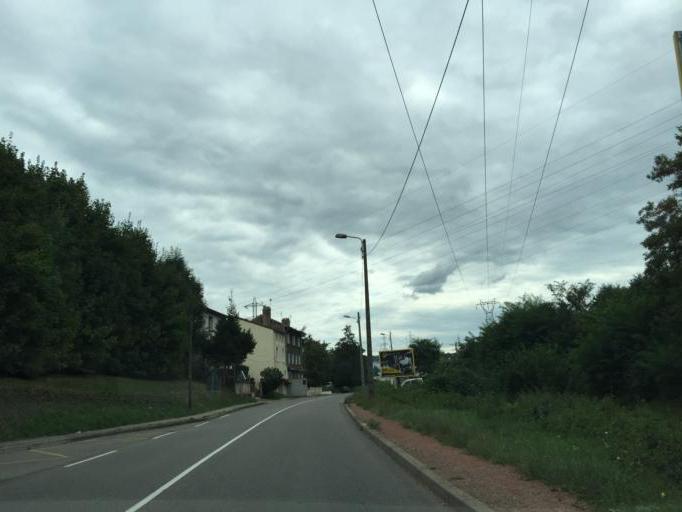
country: FR
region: Rhone-Alpes
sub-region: Departement de la Loire
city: La Talaudiere
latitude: 45.4680
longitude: 4.4119
